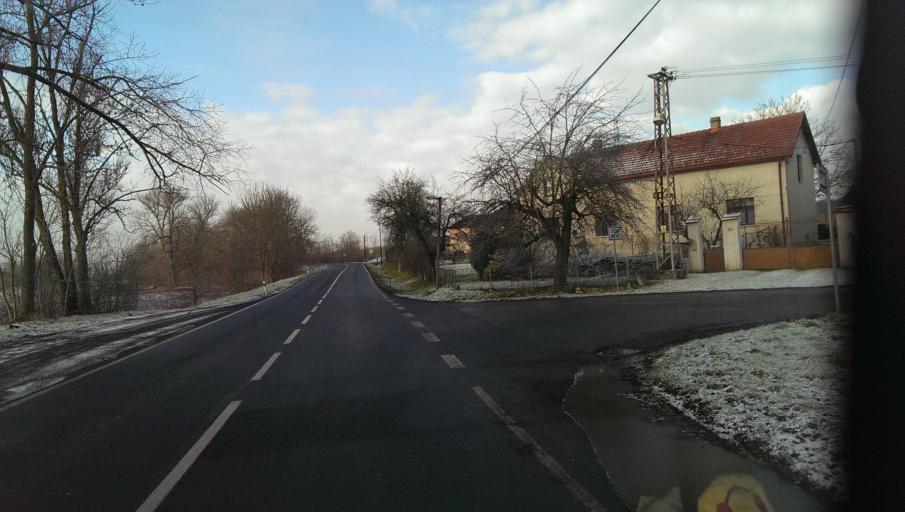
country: CZ
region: Ustecky
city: Budyne nad Ohri
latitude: 50.4111
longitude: 14.1149
